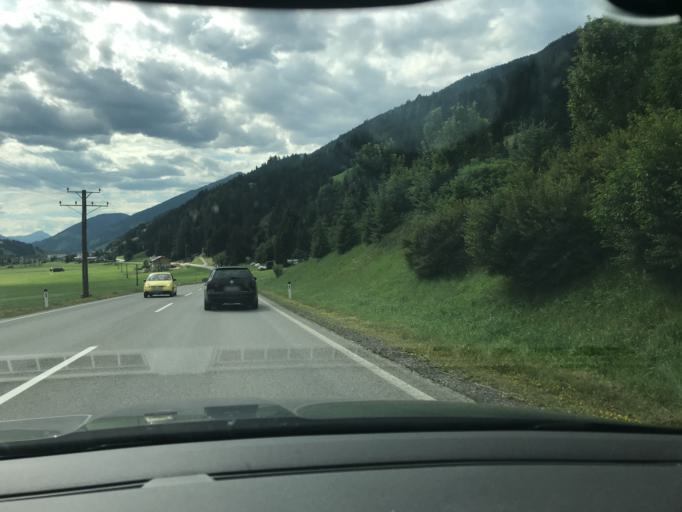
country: AT
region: Tyrol
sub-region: Politischer Bezirk Lienz
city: Strassen
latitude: 46.7495
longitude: 12.4853
